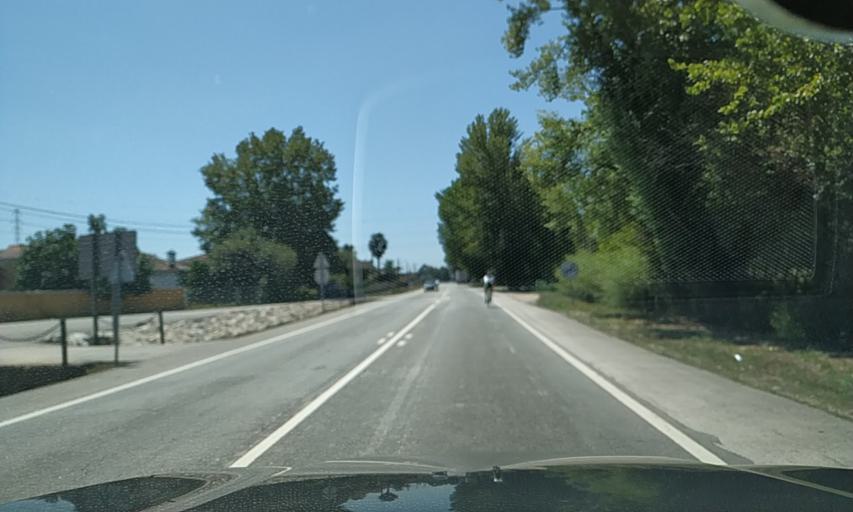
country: PT
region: Aveiro
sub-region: Anadia
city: Sangalhos
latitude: 40.4739
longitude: -8.4540
